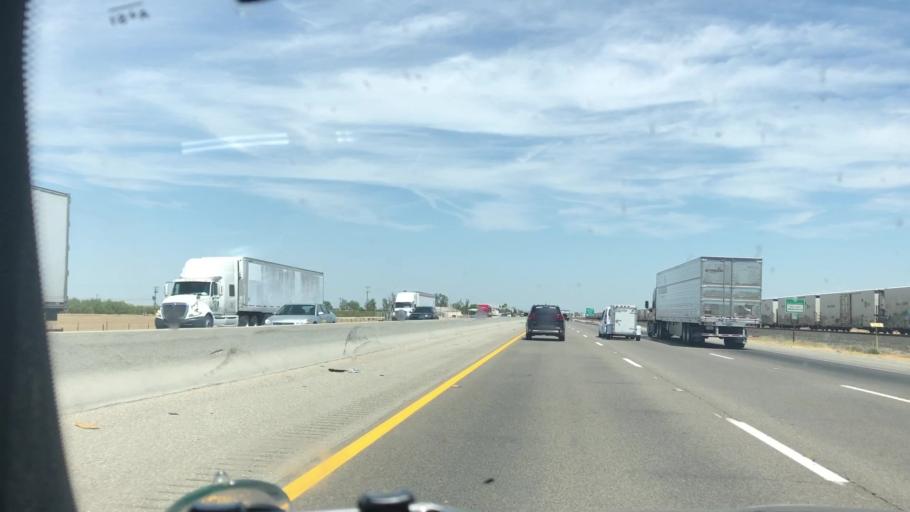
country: US
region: California
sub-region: Kern County
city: Delano
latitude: 35.7259
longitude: -119.2383
